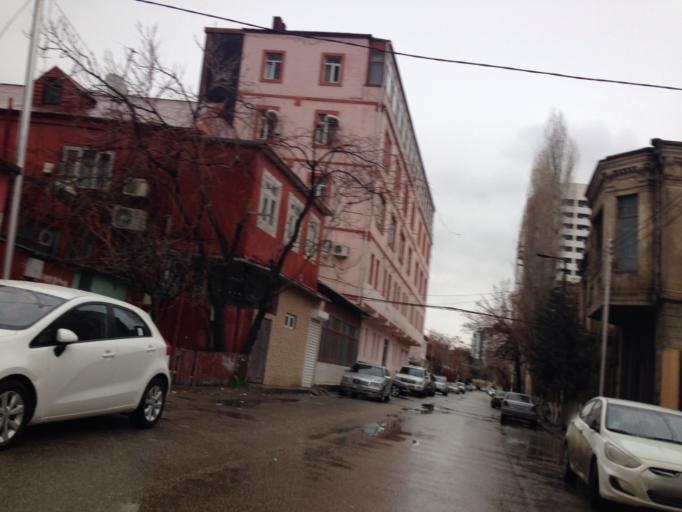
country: AZ
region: Baki
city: Baku
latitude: 40.3818
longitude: 49.8625
